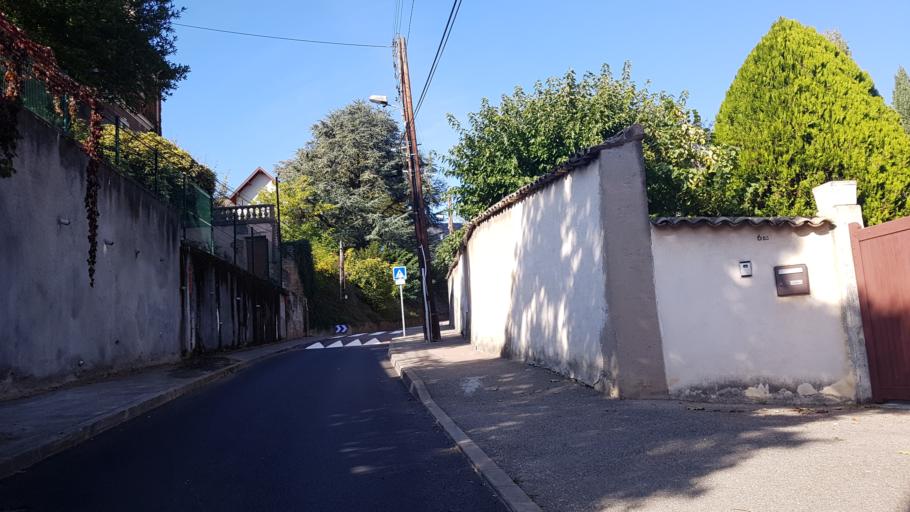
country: FR
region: Rhone-Alpes
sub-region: Departement du Rhone
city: Ecully
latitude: 45.7793
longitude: 4.7912
